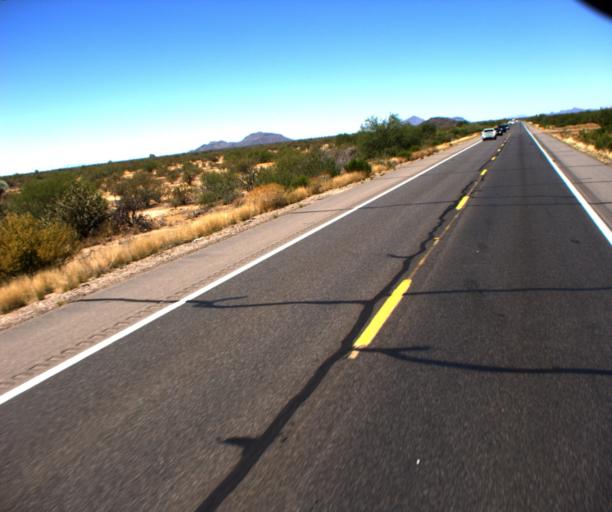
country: US
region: Arizona
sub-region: Yavapai County
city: Congress
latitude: 34.1616
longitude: -113.0055
